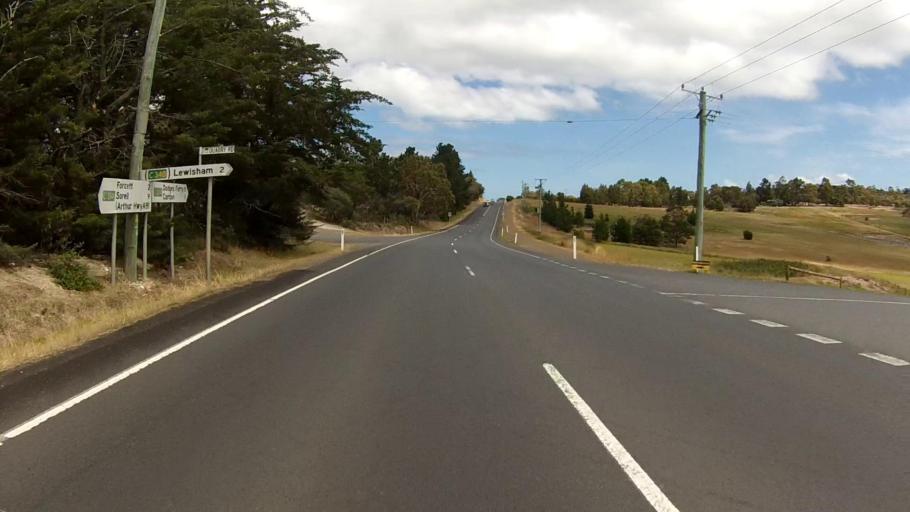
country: AU
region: Tasmania
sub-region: Sorell
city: Sorell
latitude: -42.8207
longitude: 147.6242
